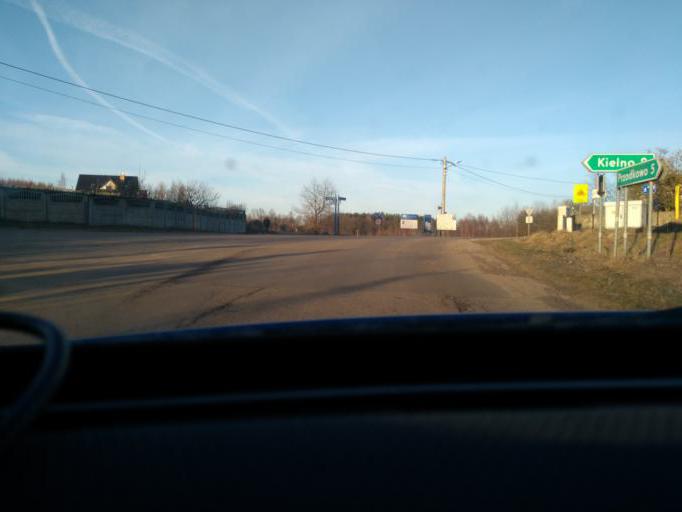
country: PL
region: Pomeranian Voivodeship
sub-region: Powiat kartuski
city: Przodkowo
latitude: 54.4139
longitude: 18.3130
